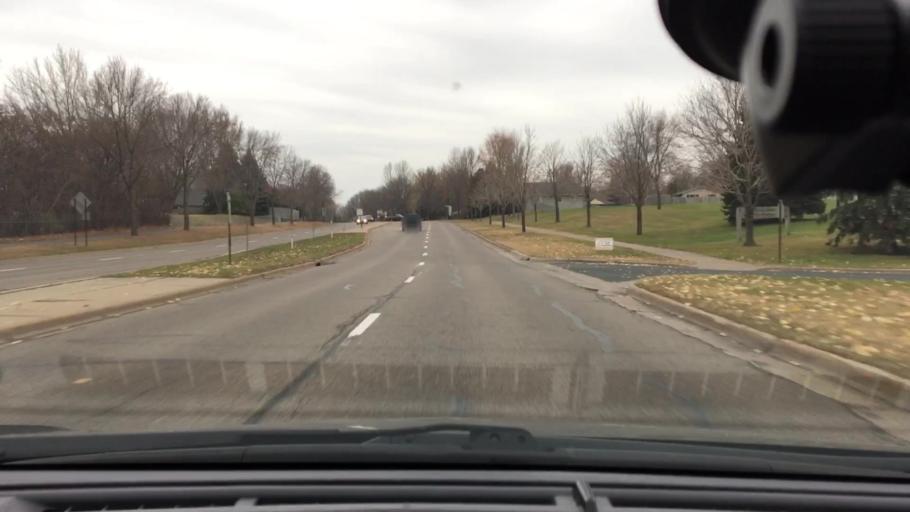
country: US
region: Minnesota
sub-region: Hennepin County
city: Maple Grove
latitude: 45.1153
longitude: -93.4521
